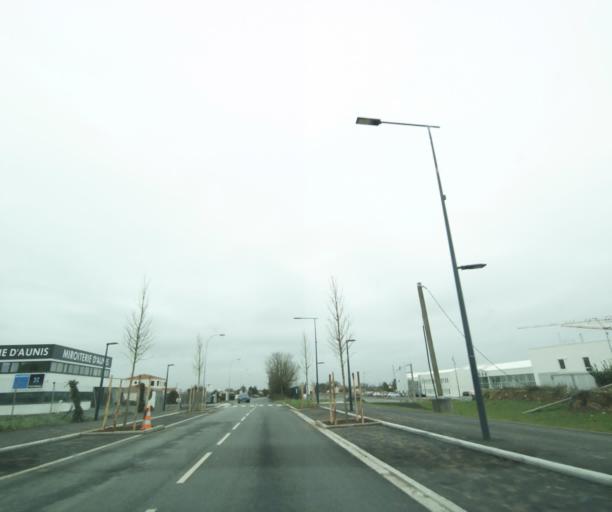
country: FR
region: Poitou-Charentes
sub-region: Departement de la Charente-Maritime
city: Lagord
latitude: 46.1858
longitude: -1.1481
